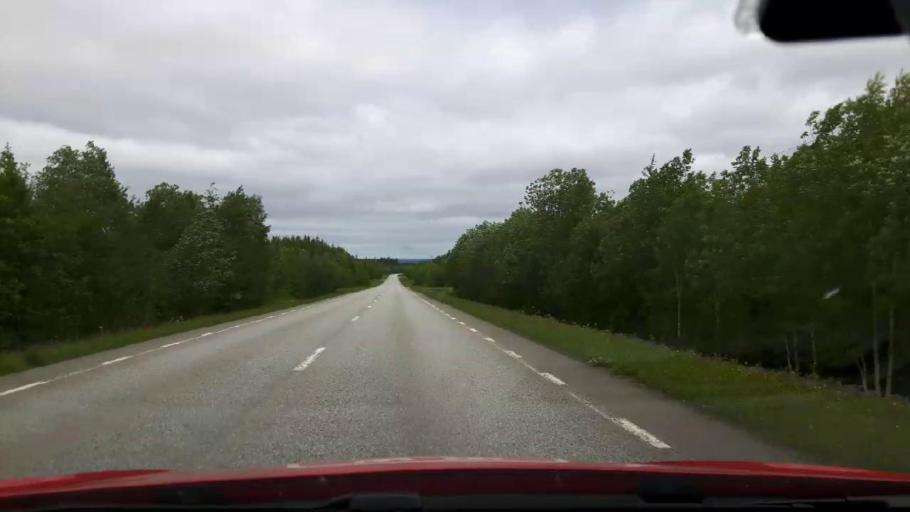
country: SE
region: Jaemtland
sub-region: Krokoms Kommun
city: Krokom
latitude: 63.5568
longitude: 14.6012
